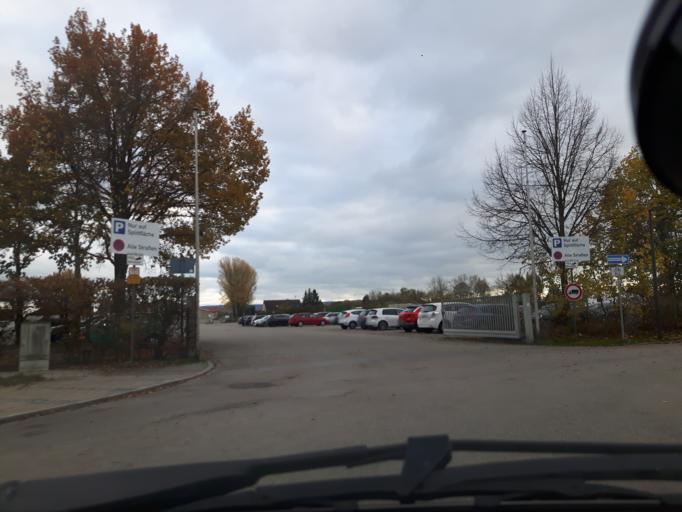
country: DE
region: Bavaria
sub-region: Regierungsbezirk Mittelfranken
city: Gunzenhausen
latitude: 49.1098
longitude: 10.7558
